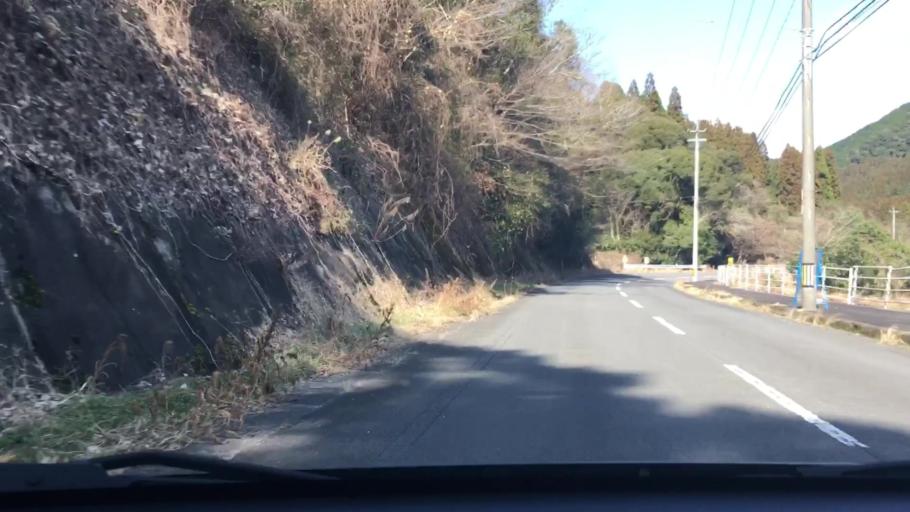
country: JP
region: Kagoshima
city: Ijuin
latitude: 31.7457
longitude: 130.4092
